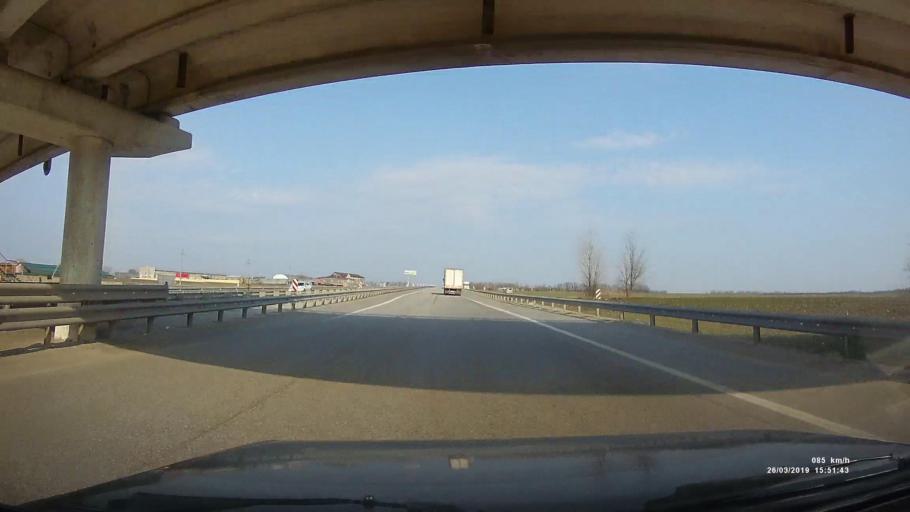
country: RU
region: Rostov
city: Kalinin
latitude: 47.2702
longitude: 39.5099
